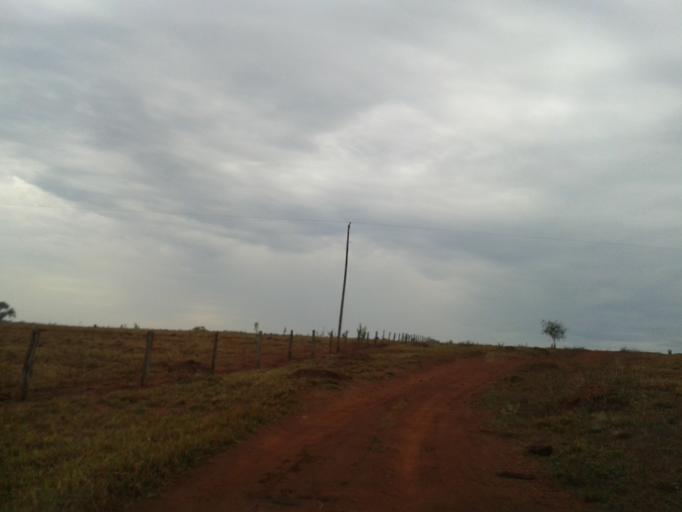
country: BR
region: Minas Gerais
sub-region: Santa Vitoria
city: Santa Vitoria
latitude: -18.8647
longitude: -49.8247
